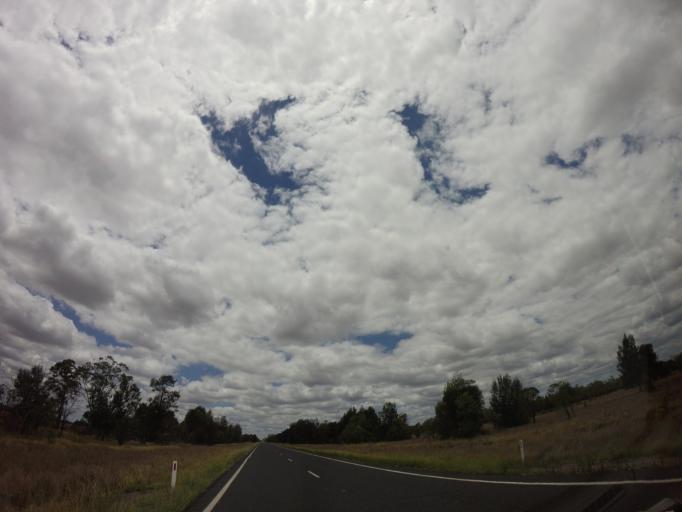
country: AU
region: Queensland
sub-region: Goondiwindi
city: Goondiwindi
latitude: -28.1687
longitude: 150.5910
